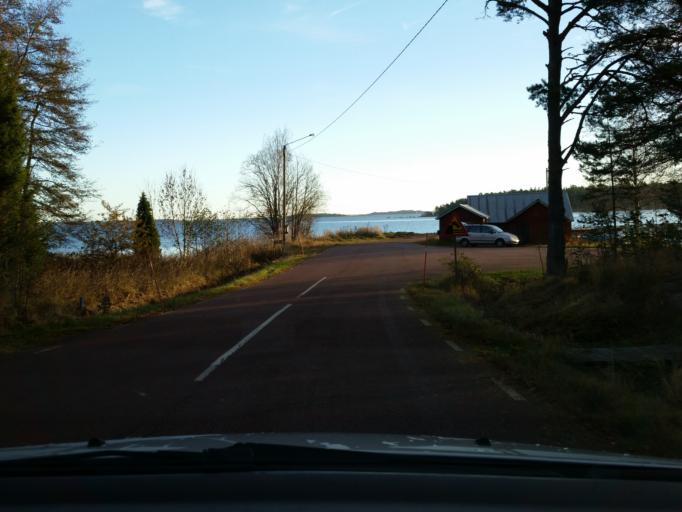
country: AX
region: Alands landsbygd
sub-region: Sund
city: Sund
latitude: 60.3103
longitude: 20.1920
